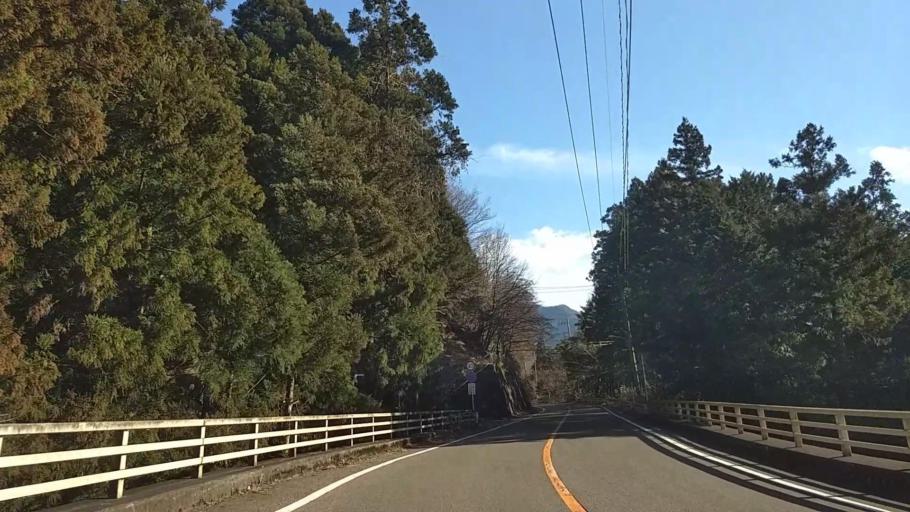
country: JP
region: Yamanashi
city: Uenohara
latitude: 35.5344
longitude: 139.0929
